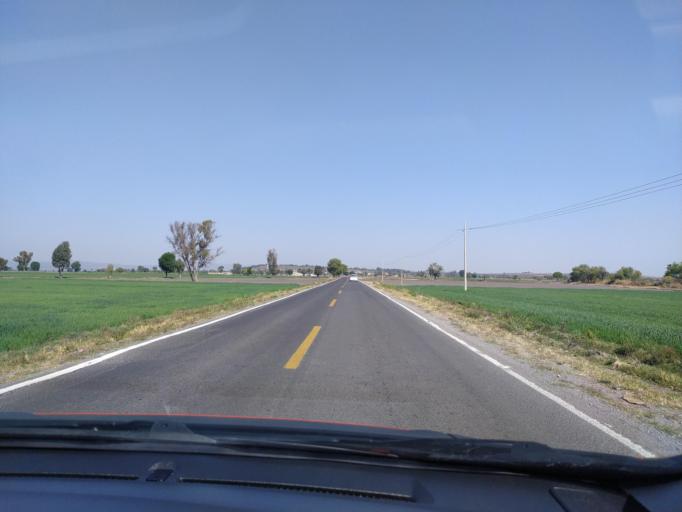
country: MX
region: Guanajuato
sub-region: San Francisco del Rincon
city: San Ignacio de Hidalgo
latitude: 20.8399
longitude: -101.8469
